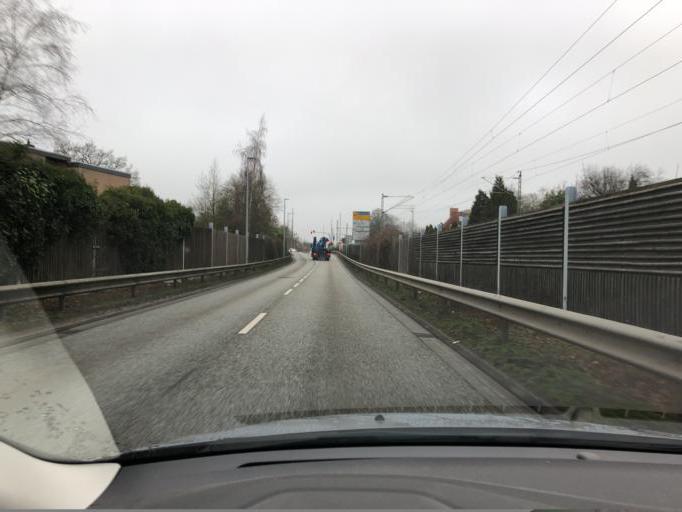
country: DE
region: Lower Saxony
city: Bad Zwischenahn
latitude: 53.1813
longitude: 8.0110
